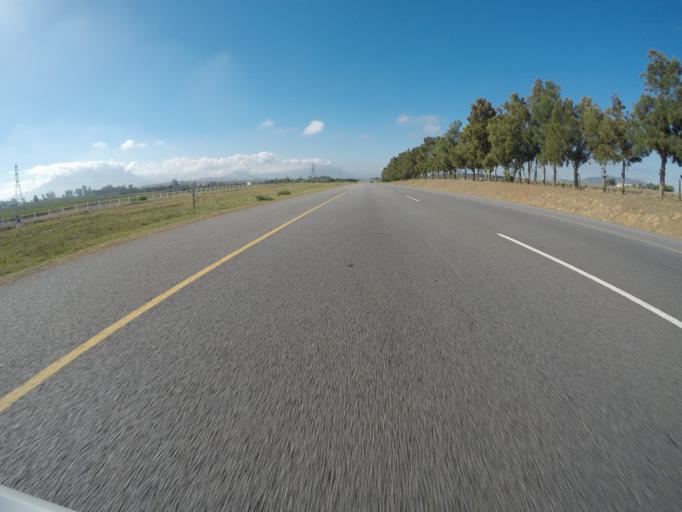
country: ZA
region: Western Cape
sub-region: City of Cape Town
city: Kraaifontein
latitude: -33.8476
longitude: 18.8038
